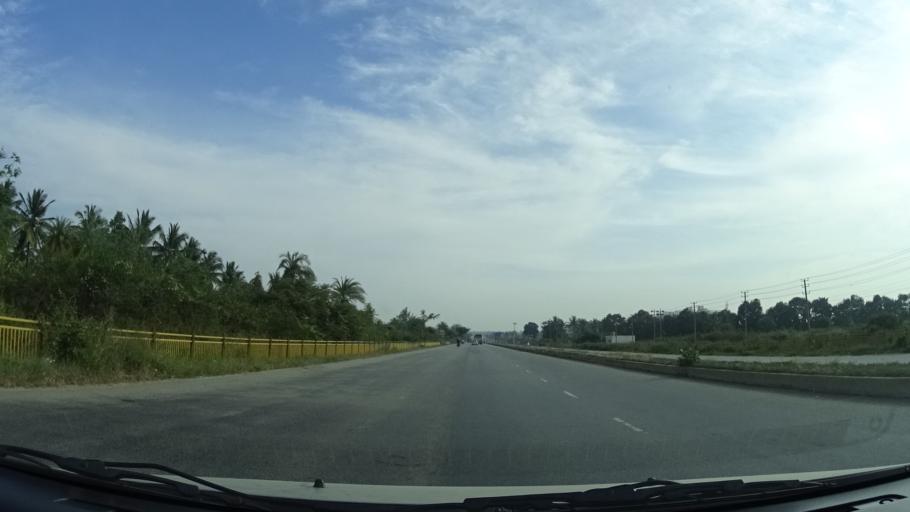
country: IN
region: Karnataka
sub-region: Bangalore Rural
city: Devanhalli
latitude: 13.2283
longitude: 77.6890
